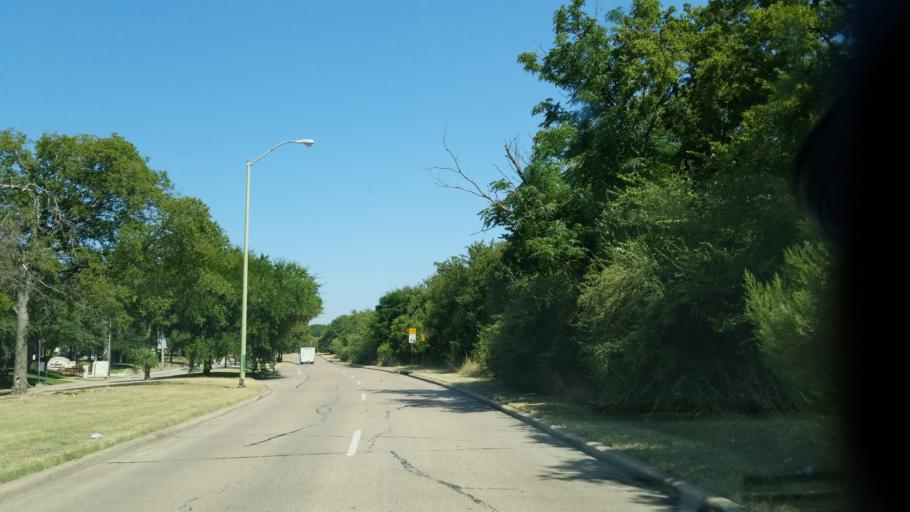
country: US
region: Texas
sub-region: Dallas County
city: Cockrell Hill
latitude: 32.7276
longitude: -96.9086
